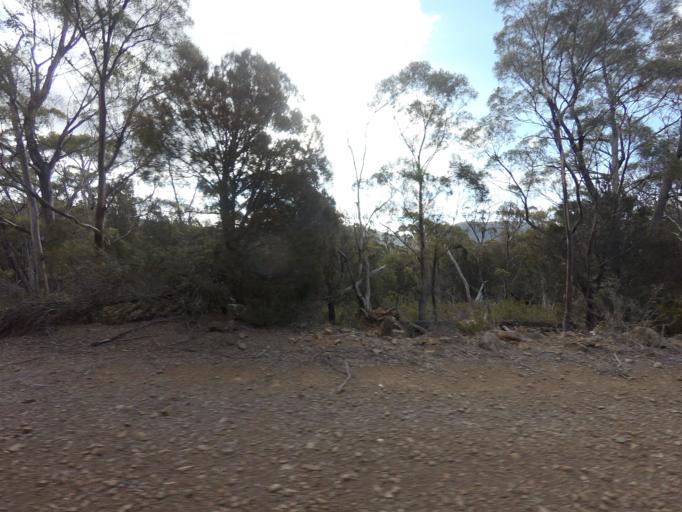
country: AU
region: Tasmania
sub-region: Break O'Day
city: St Helens
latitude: -41.8584
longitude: 148.0240
